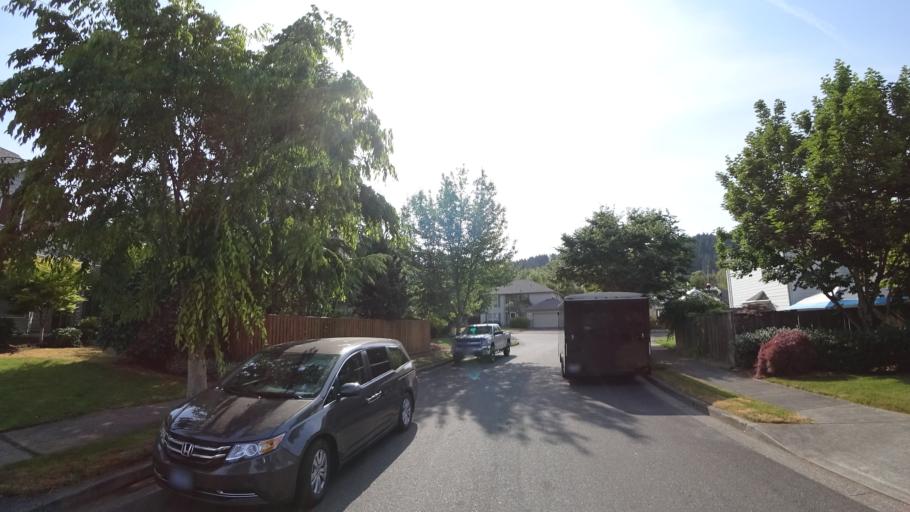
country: US
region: Oregon
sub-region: Clackamas County
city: Happy Valley
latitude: 45.4523
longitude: -122.5177
